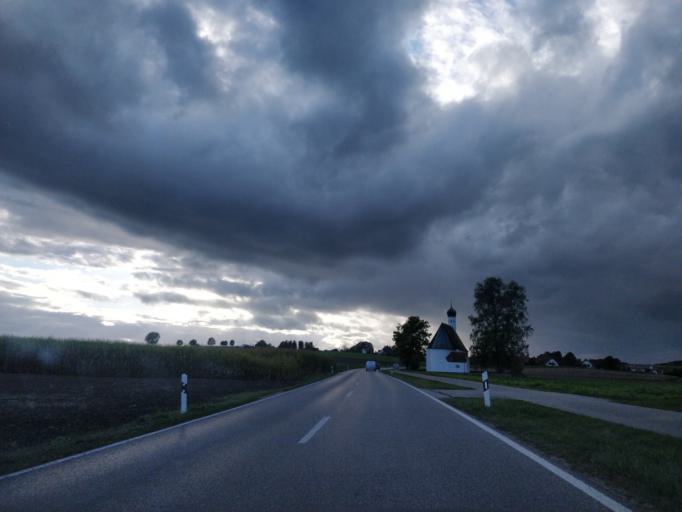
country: DE
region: Bavaria
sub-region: Swabia
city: Ried
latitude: 48.2923
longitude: 11.0608
